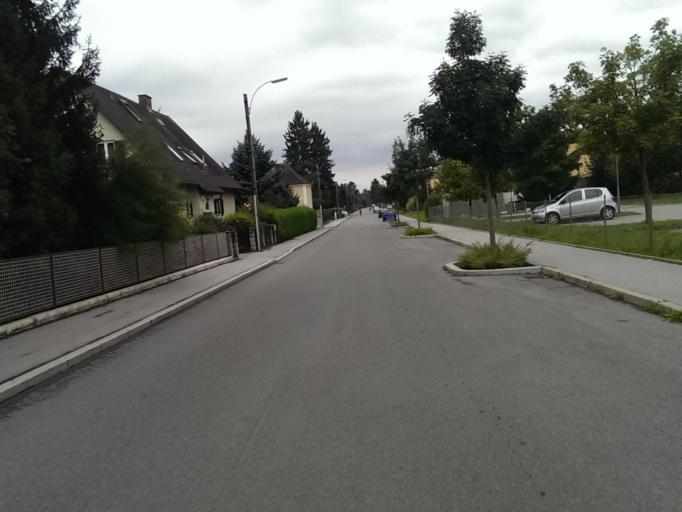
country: AT
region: Styria
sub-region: Politischer Bezirk Graz-Umgebung
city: Raaba
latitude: 47.0496
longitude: 15.4767
